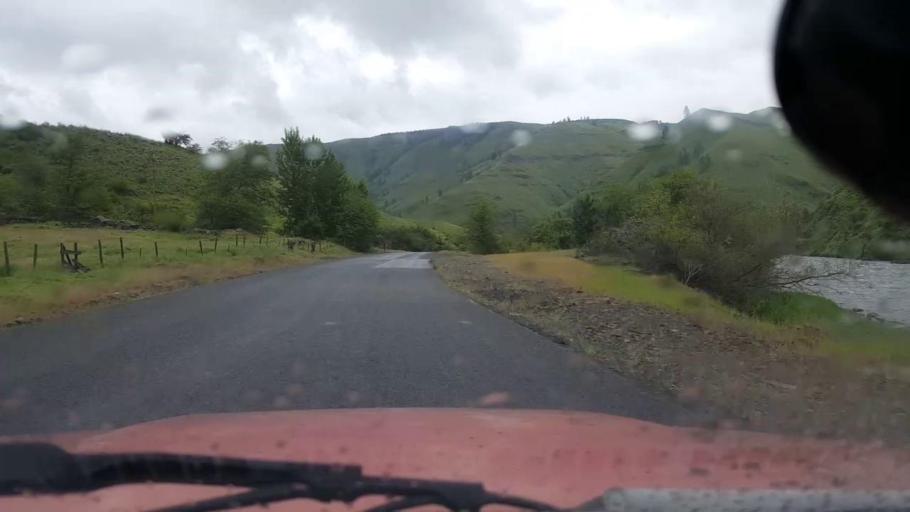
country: US
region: Washington
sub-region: Asotin County
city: Asotin
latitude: 46.0332
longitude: -117.3203
